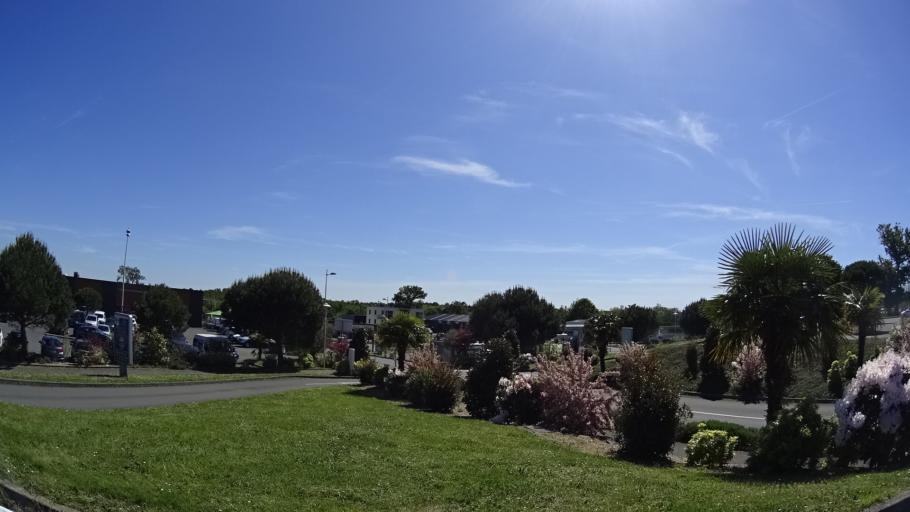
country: FR
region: Brittany
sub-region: Departement d'Ille-et-Vilaine
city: Melesse
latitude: 48.2148
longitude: -1.7027
